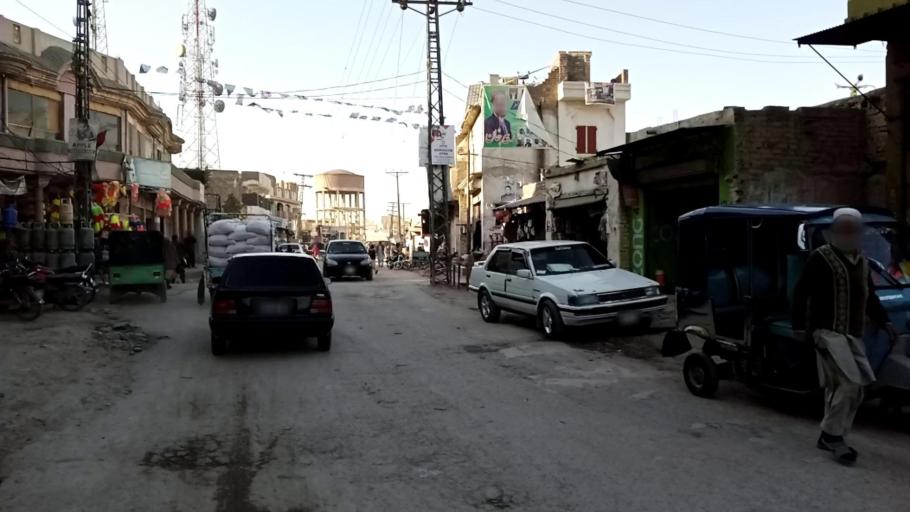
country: PK
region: Khyber Pakhtunkhwa
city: Peshawar
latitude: 34.0563
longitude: 71.5411
